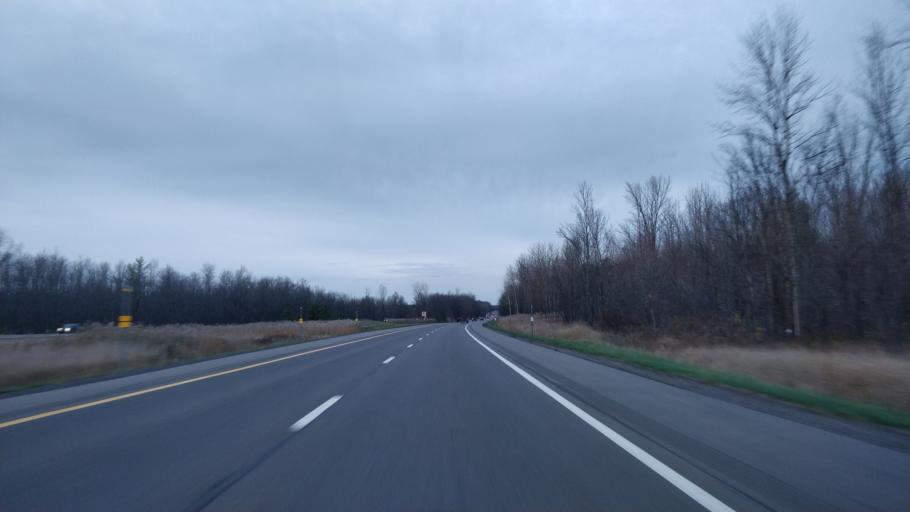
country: US
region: New York
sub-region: Oswego County
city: Central Square
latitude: 43.3435
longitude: -76.1226
